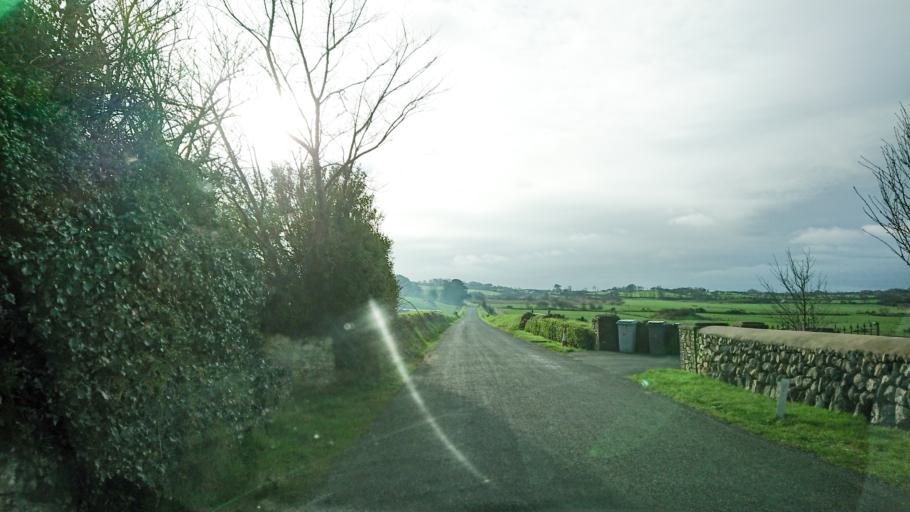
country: IE
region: Munster
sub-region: Waterford
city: Tra Mhor
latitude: 52.1652
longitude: -7.1872
